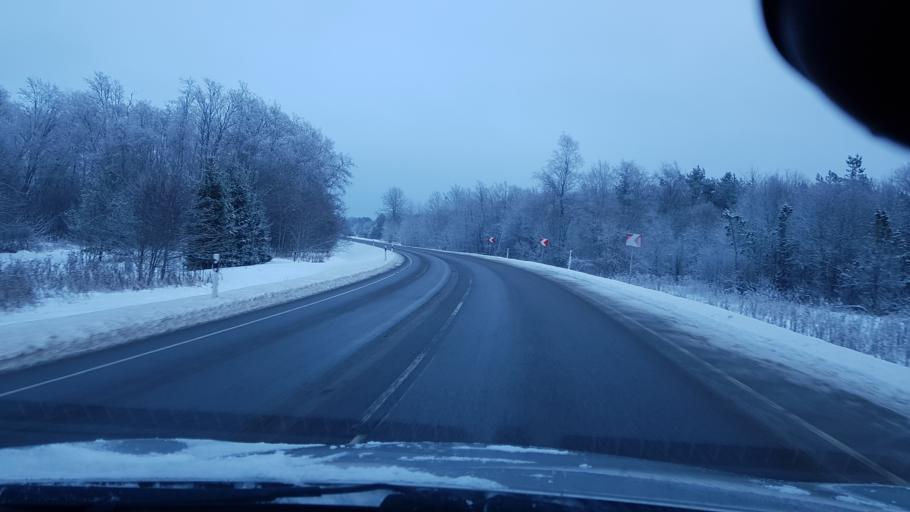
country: EE
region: Harju
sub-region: Paldiski linn
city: Paldiski
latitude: 59.3398
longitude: 24.2030
